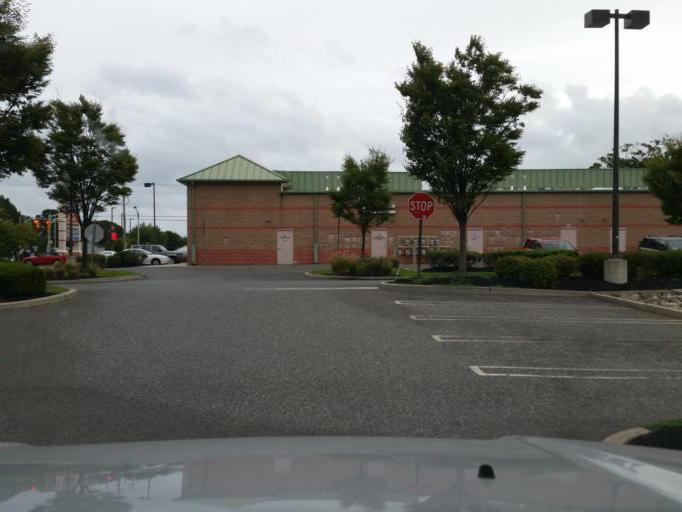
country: US
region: New Jersey
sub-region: Cape May County
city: Rio Grande
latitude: 39.0174
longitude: -74.8747
